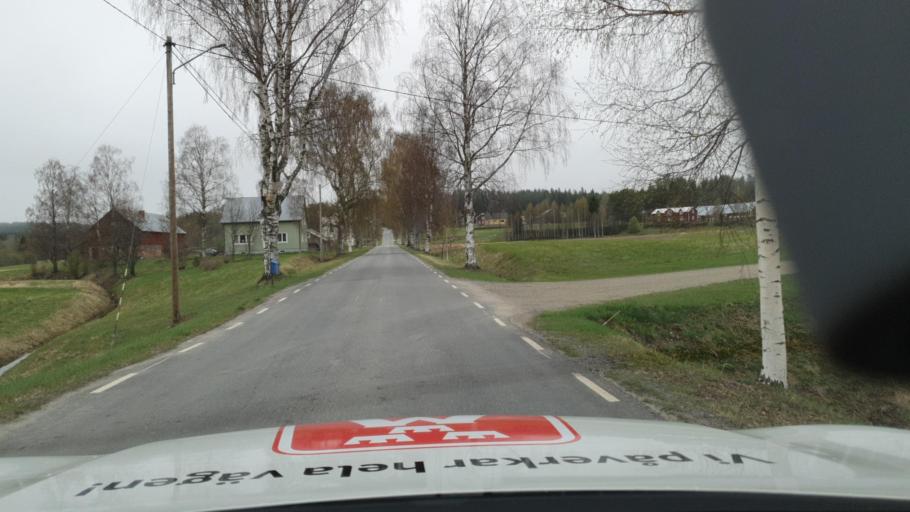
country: SE
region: Vaesterbotten
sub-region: Nordmalings Kommun
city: Nordmaling
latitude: 63.7253
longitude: 19.5131
